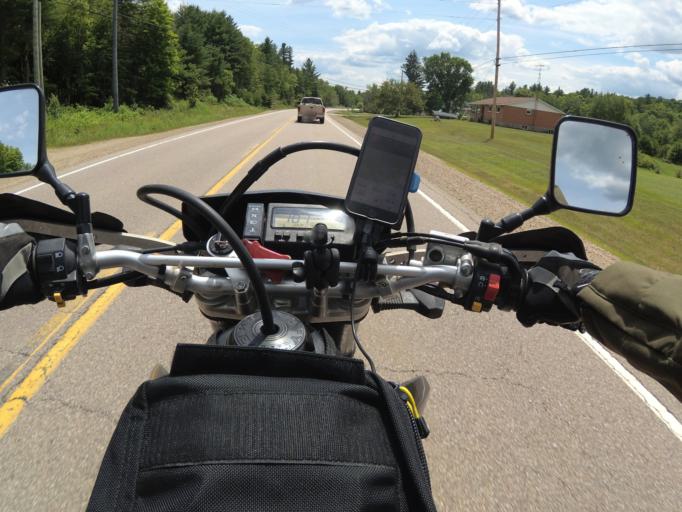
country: CA
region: Ontario
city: Greater Napanee
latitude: 44.8455
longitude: -77.1809
